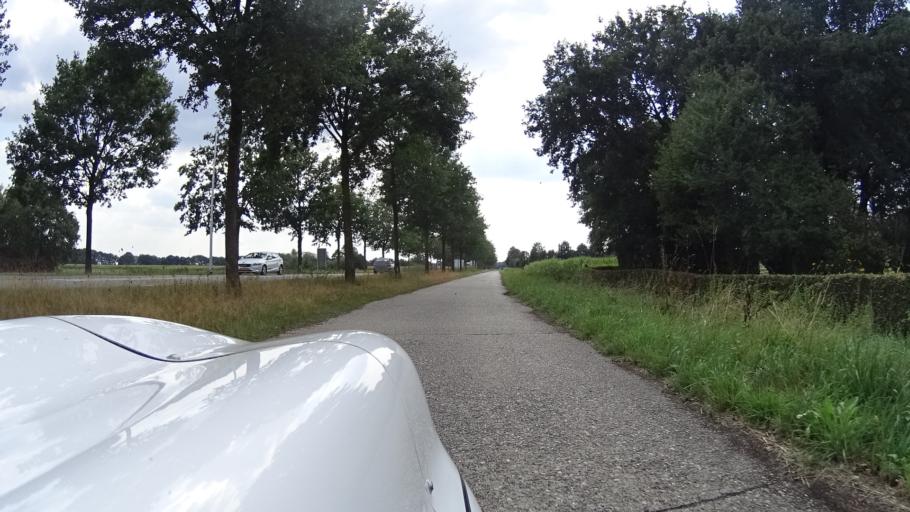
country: NL
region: North Brabant
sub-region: Gemeente Sint Anthonis
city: Sint Anthonis
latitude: 51.6121
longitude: 5.8660
